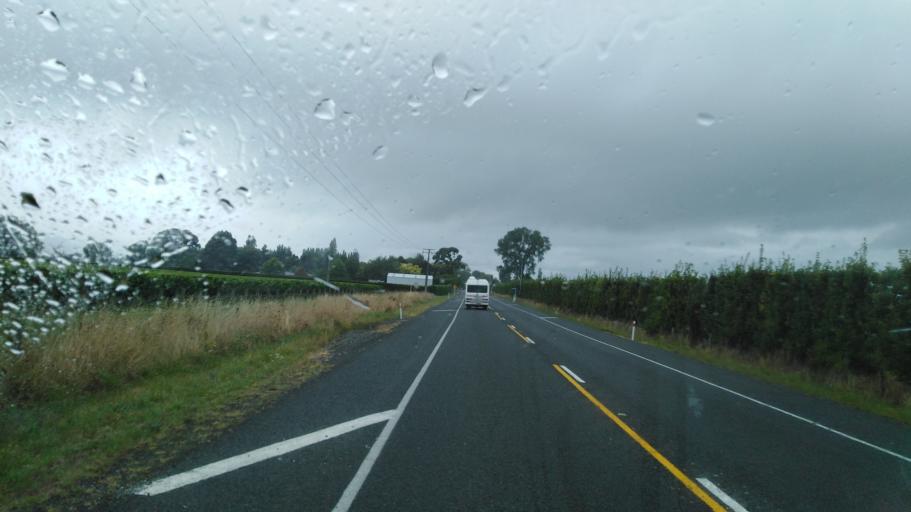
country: NZ
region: Marlborough
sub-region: Marlborough District
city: Blenheim
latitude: -41.4598
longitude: 173.9442
